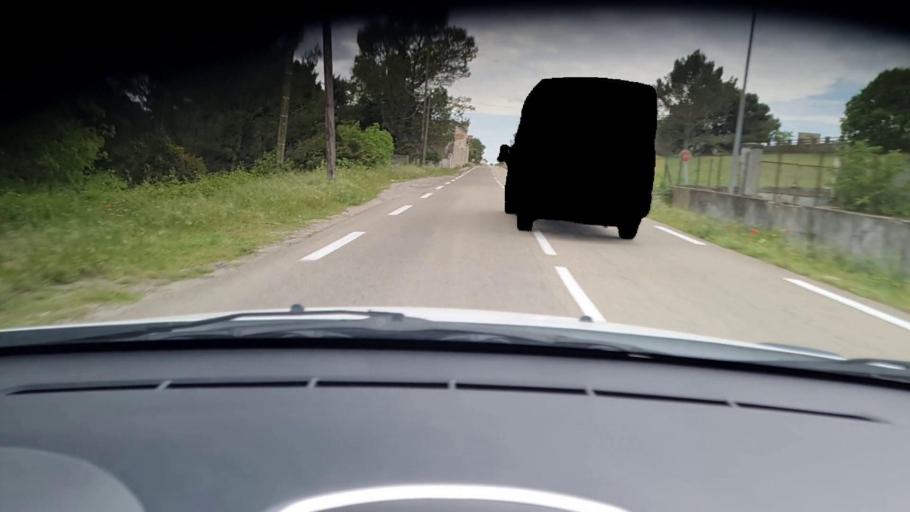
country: FR
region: Languedoc-Roussillon
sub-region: Departement du Gard
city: Poulx
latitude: 43.8820
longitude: 4.3790
